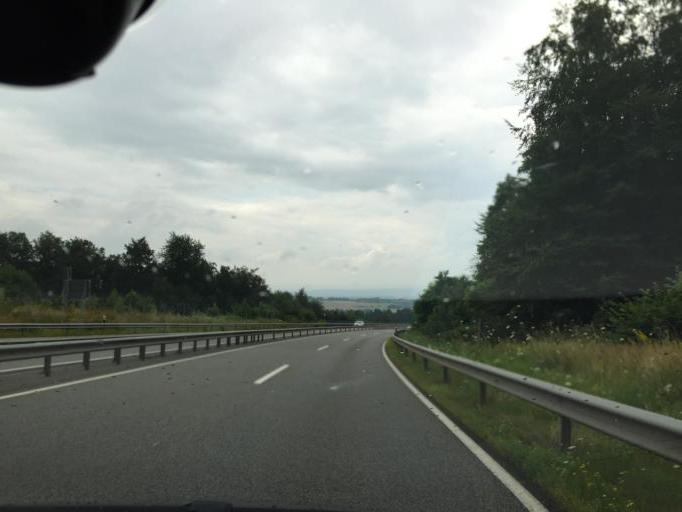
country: DE
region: Rheinland-Pfalz
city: Rengsdorf
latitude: 50.4889
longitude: 7.4960
